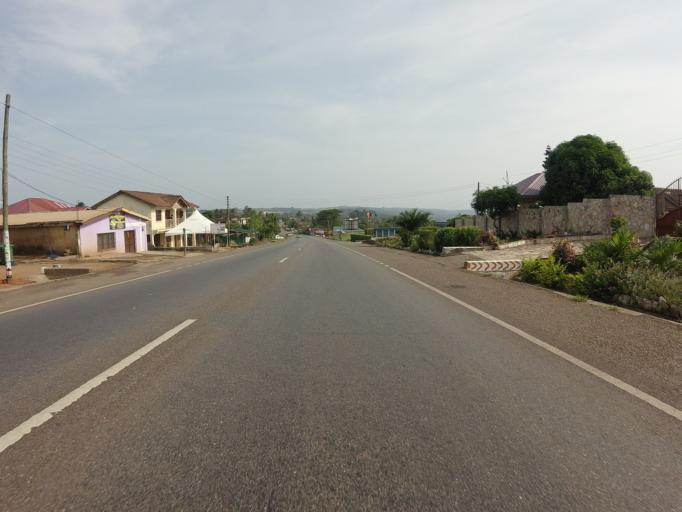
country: GH
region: Eastern
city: Aburi
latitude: 5.8677
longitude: -0.1597
